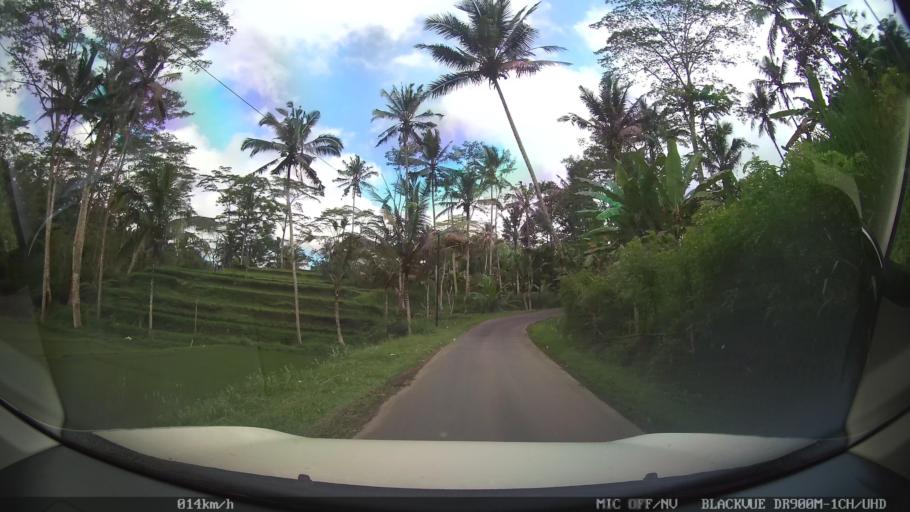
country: ID
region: Bali
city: Banjar Petak
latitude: -8.4491
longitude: 115.3261
